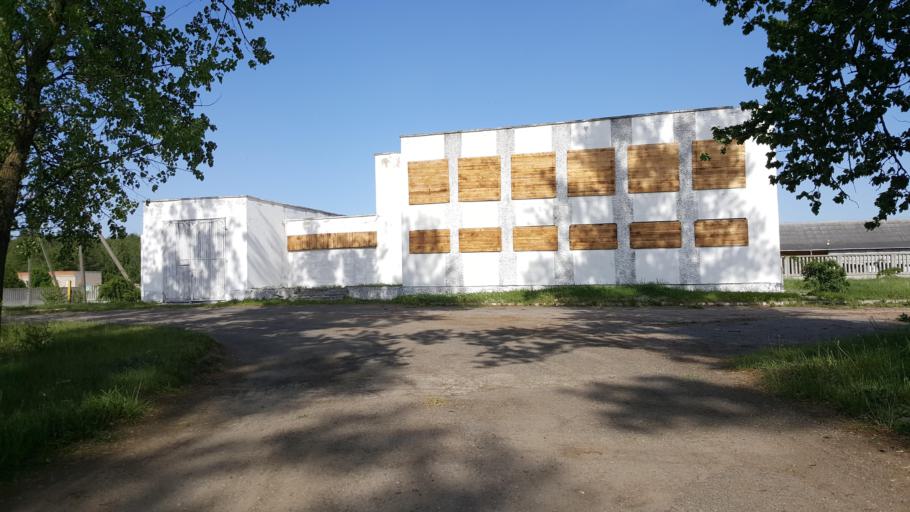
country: BY
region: Brest
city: Kamyanyets
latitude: 52.3387
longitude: 23.7932
